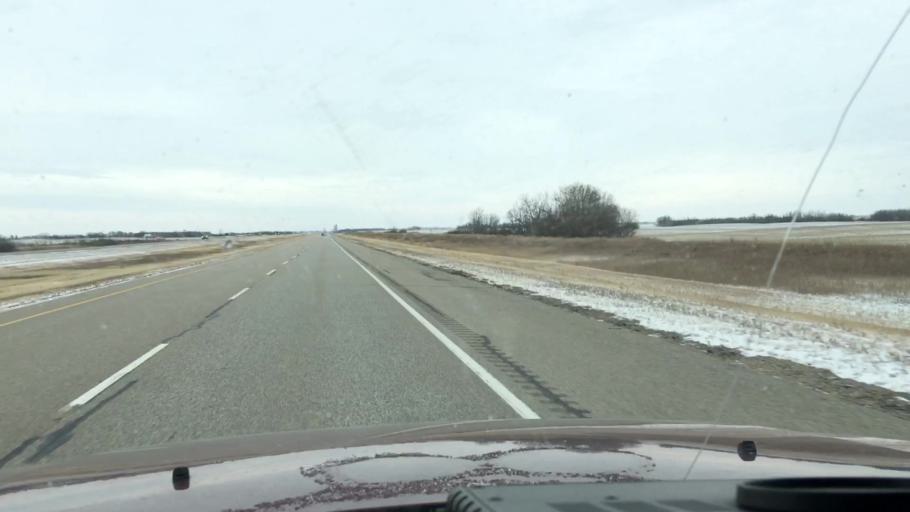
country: CA
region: Saskatchewan
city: Watrous
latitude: 51.3246
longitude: -106.0729
